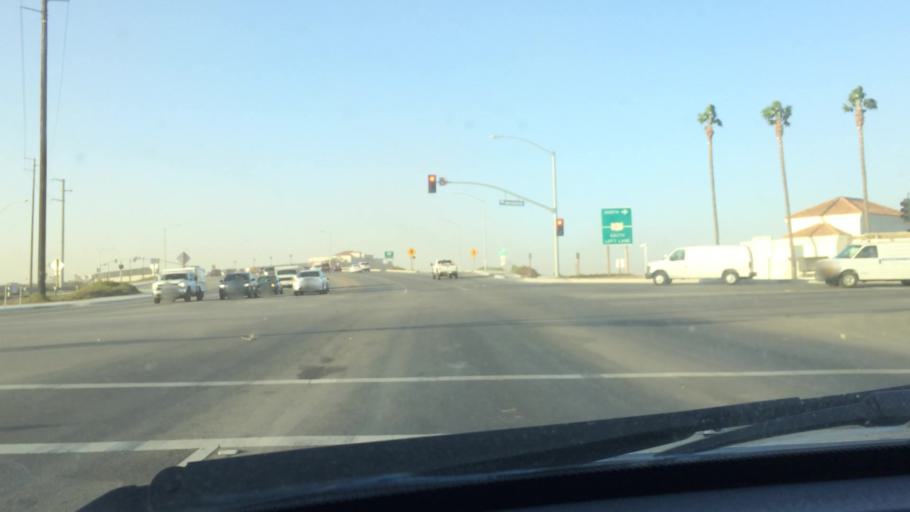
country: US
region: California
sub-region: Ventura County
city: El Rio
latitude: 34.2246
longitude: -119.1408
